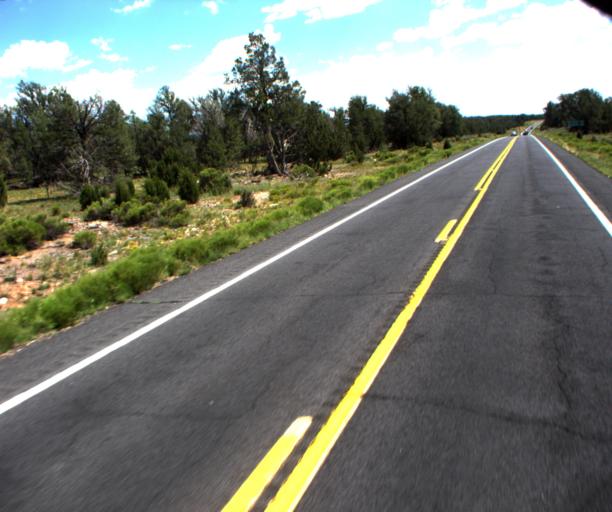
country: US
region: Arizona
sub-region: Coconino County
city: Grand Canyon Village
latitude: 35.8462
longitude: -112.1328
